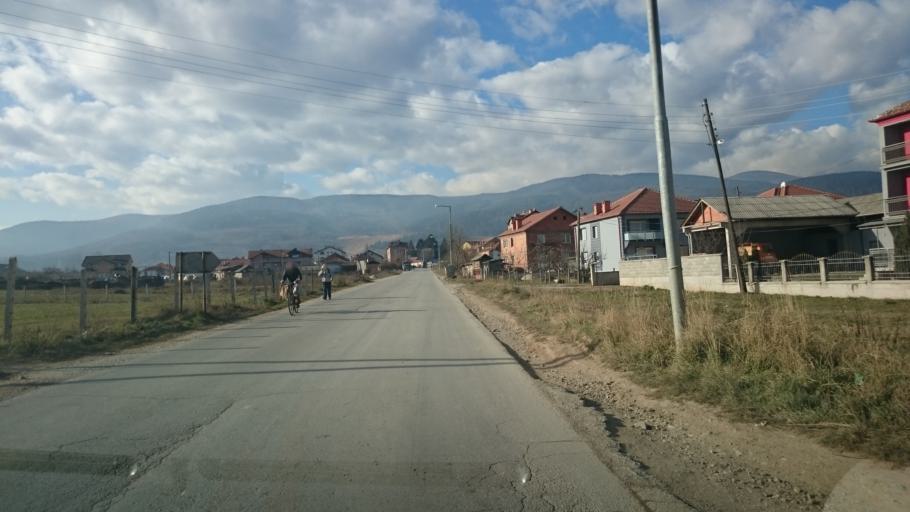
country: MK
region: Kicevo
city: Kicevo
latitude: 41.5002
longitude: 20.9567
